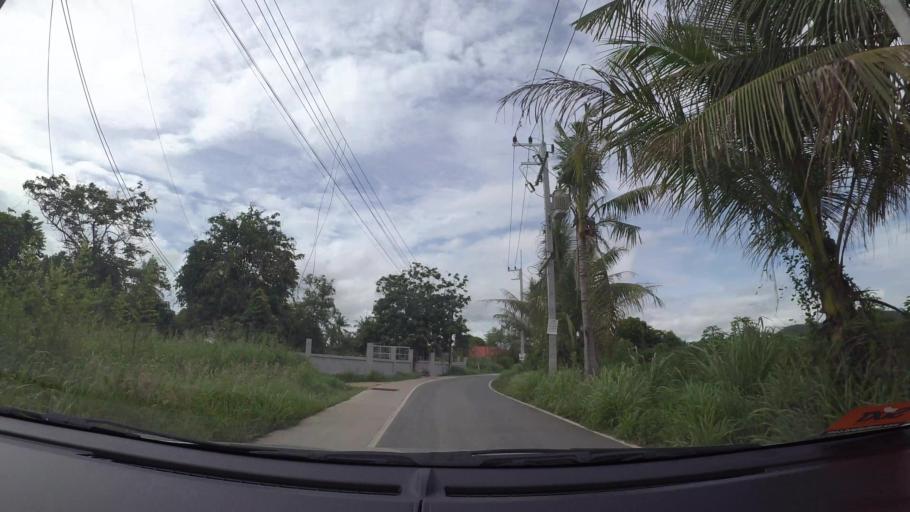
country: TH
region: Chon Buri
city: Sattahip
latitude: 12.7137
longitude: 100.9012
